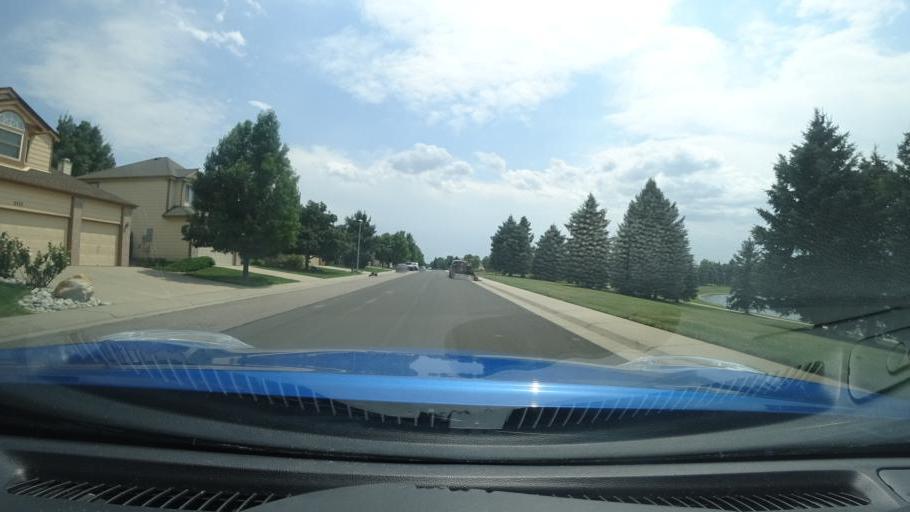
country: US
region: Colorado
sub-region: Adams County
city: Aurora
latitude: 39.6754
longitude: -104.7733
